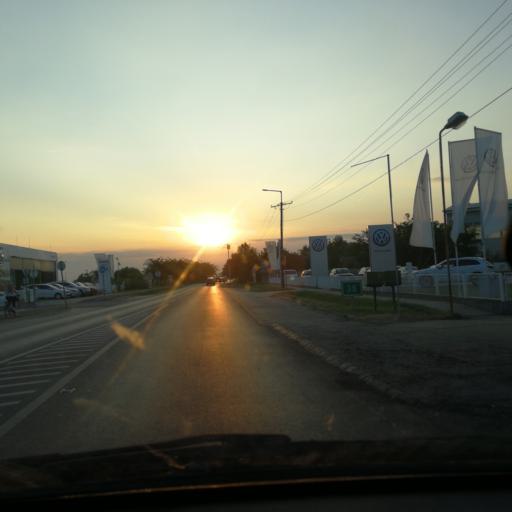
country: HU
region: Bacs-Kiskun
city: Soltvadkert
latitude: 46.5829
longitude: 19.3720
